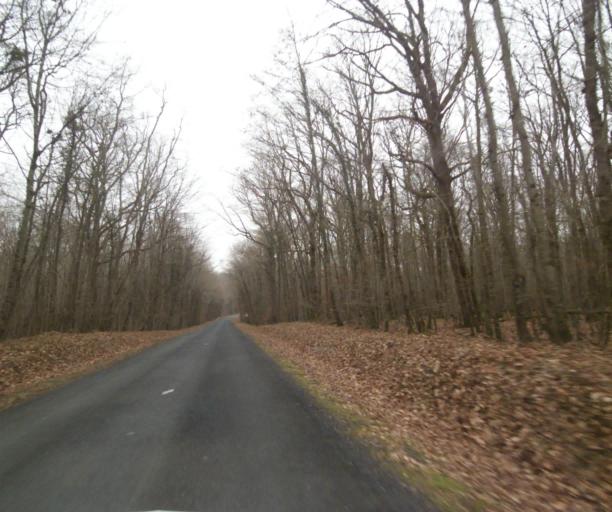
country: FR
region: Champagne-Ardenne
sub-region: Departement de la Haute-Marne
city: Bienville
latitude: 48.5611
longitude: 5.0046
